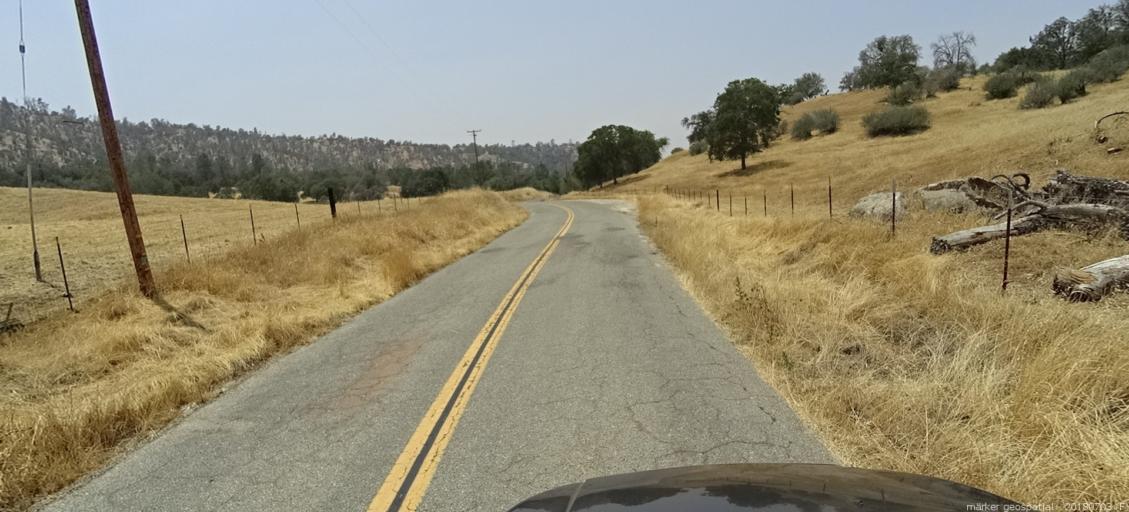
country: US
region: California
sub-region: Madera County
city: Yosemite Lakes
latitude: 37.0655
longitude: -119.6751
